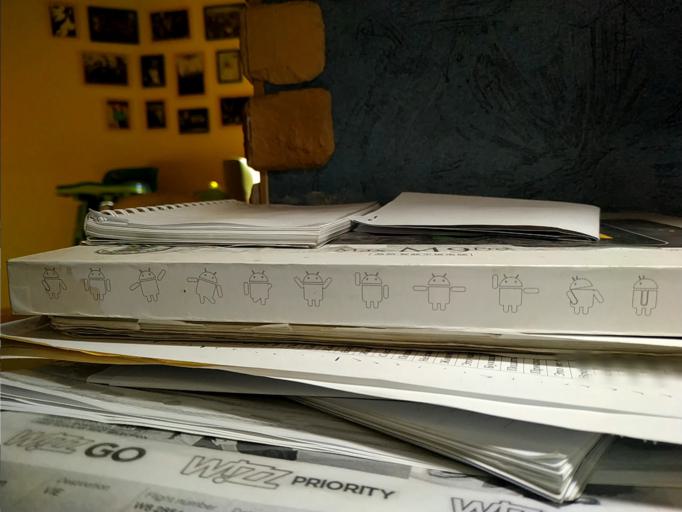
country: RU
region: Novgorod
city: Poddor'ye
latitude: 57.3281
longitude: 31.1853
